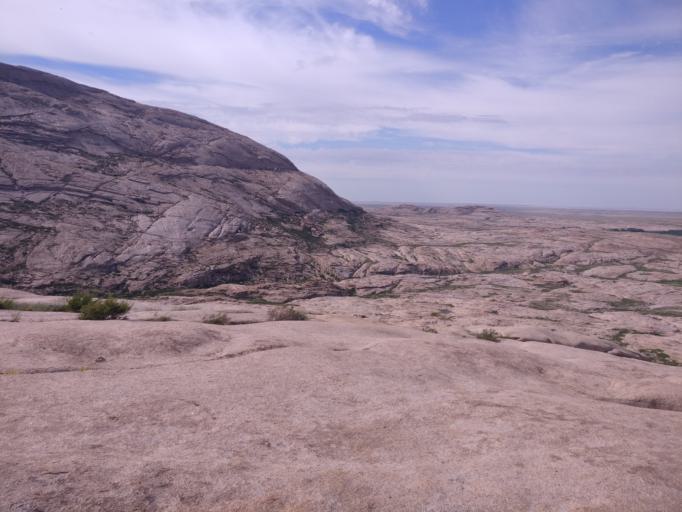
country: KZ
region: Qaraghandy
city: Balqash
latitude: 47.4385
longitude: 74.8268
